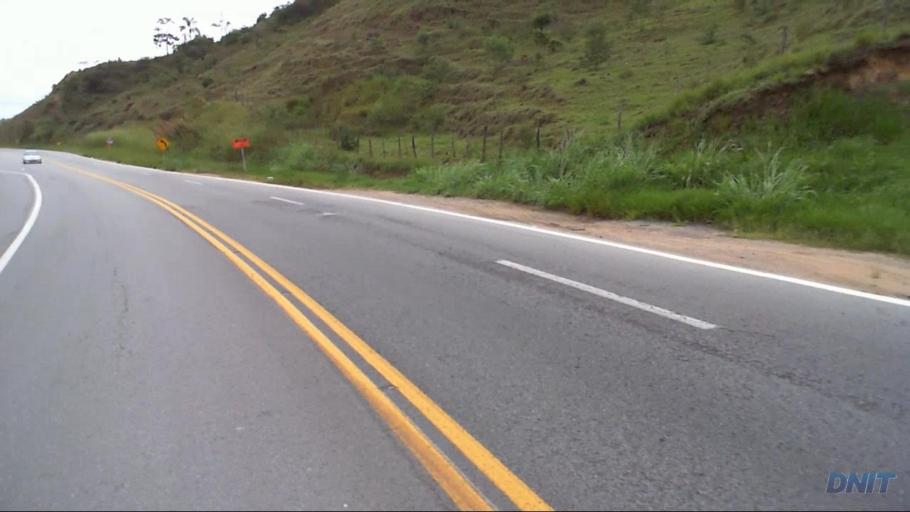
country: BR
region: Minas Gerais
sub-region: Nova Era
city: Nova Era
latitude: -19.6411
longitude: -42.9008
